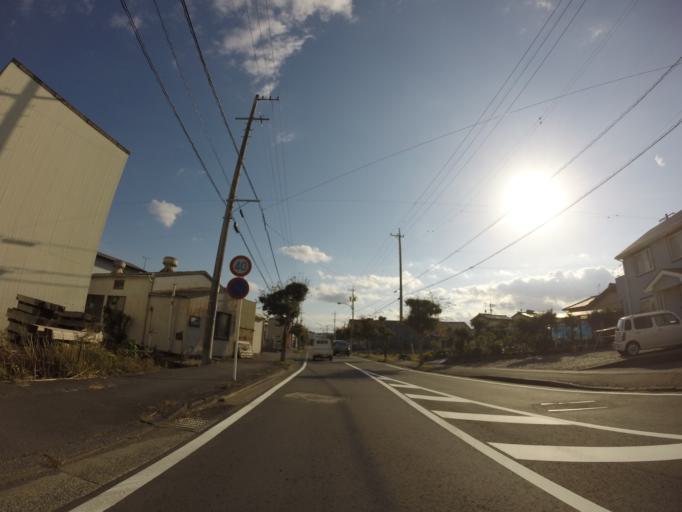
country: JP
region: Shizuoka
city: Kanaya
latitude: 34.8416
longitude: 138.1503
